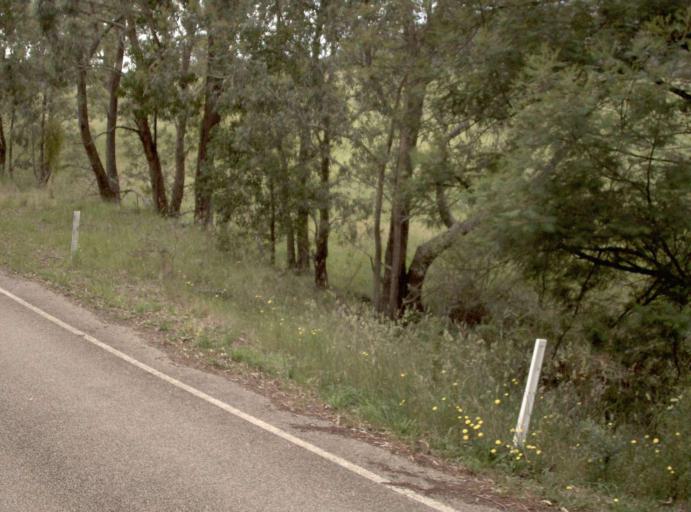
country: AU
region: Victoria
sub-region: East Gippsland
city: Bairnsdale
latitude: -37.5505
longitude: 147.1990
